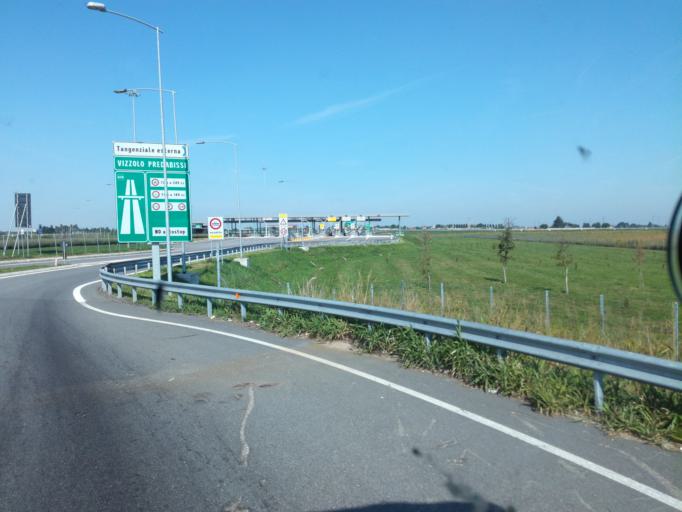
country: IT
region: Lombardy
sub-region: Provincia di Lodi
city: Sordio
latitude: 45.3460
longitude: 9.3569
